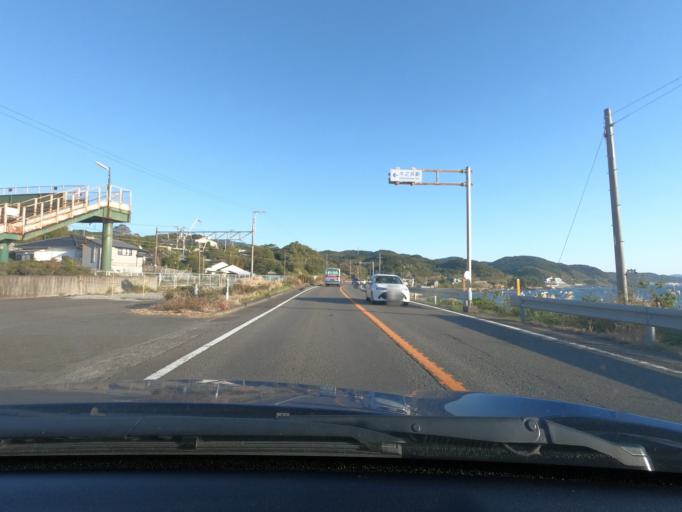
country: JP
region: Kagoshima
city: Akune
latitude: 31.9739
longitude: 130.2069
